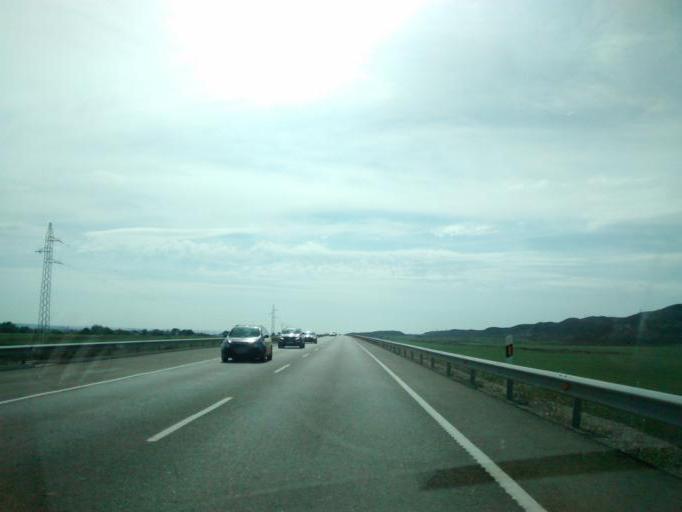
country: ES
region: Aragon
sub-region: Provincia de Zaragoza
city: El Burgo de Ebro
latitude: 41.5577
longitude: -0.7240
